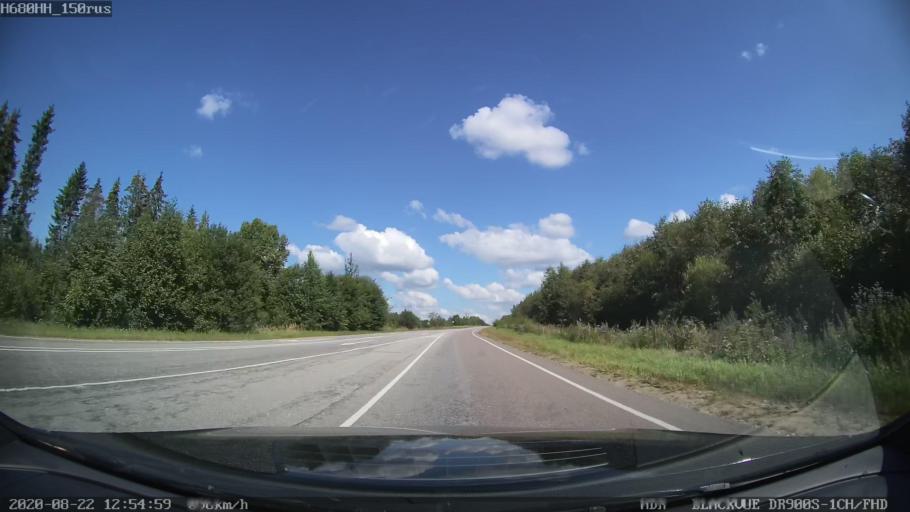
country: RU
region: Tverskaya
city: Rameshki
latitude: 57.5387
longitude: 36.2925
